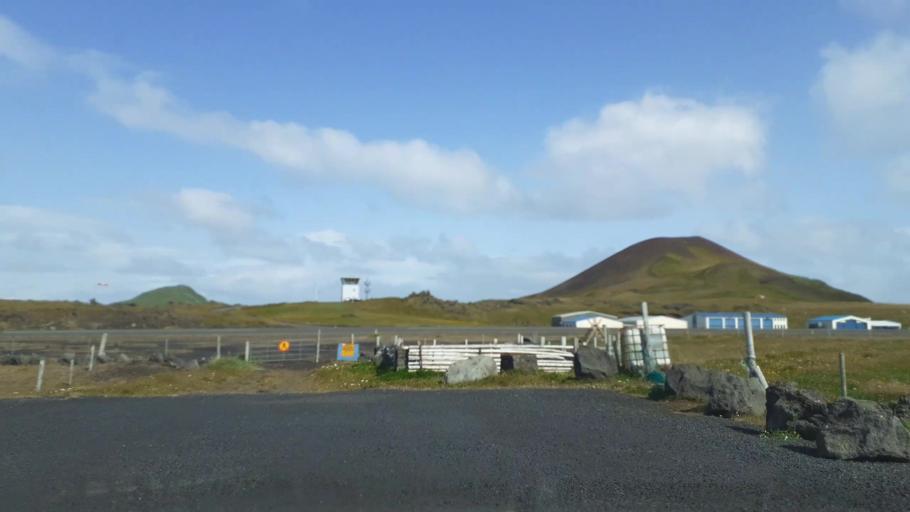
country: IS
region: South
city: Vestmannaeyjar
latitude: 63.4235
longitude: -20.2767
